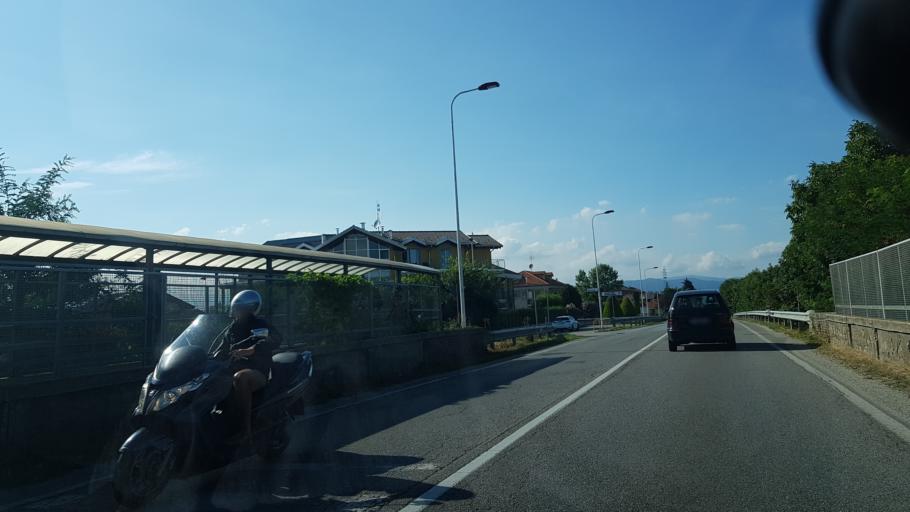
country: IT
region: Piedmont
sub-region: Provincia di Cuneo
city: Cuneo
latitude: 44.4162
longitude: 7.5488
